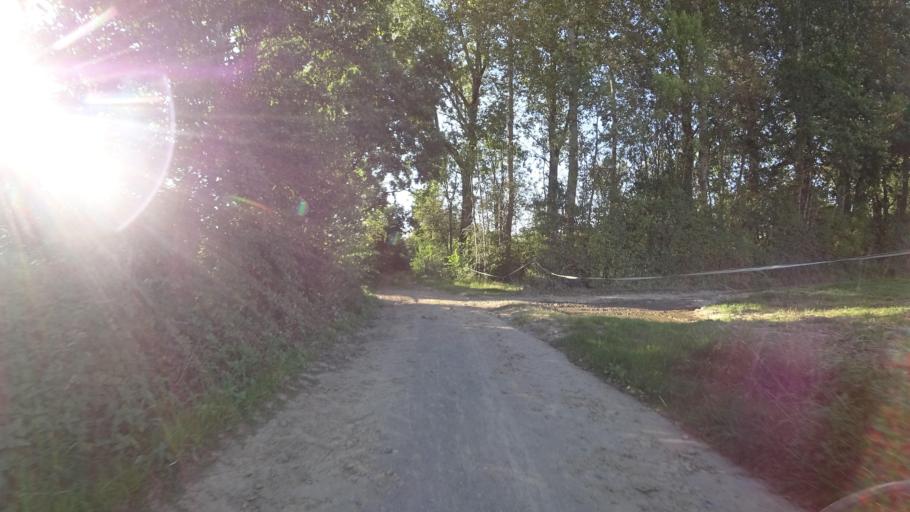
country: BE
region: Wallonia
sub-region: Province du Brabant Wallon
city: Perwez
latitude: 50.5962
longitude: 4.7600
